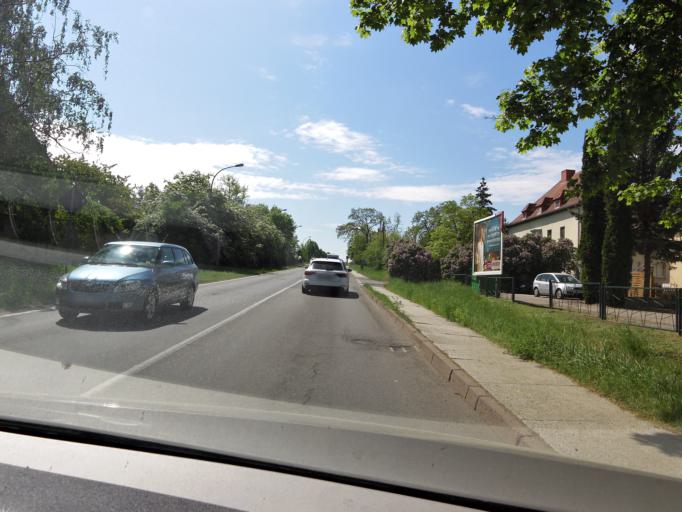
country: DE
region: Thuringia
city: Bad Langensalza
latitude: 51.1009
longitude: 10.6457
